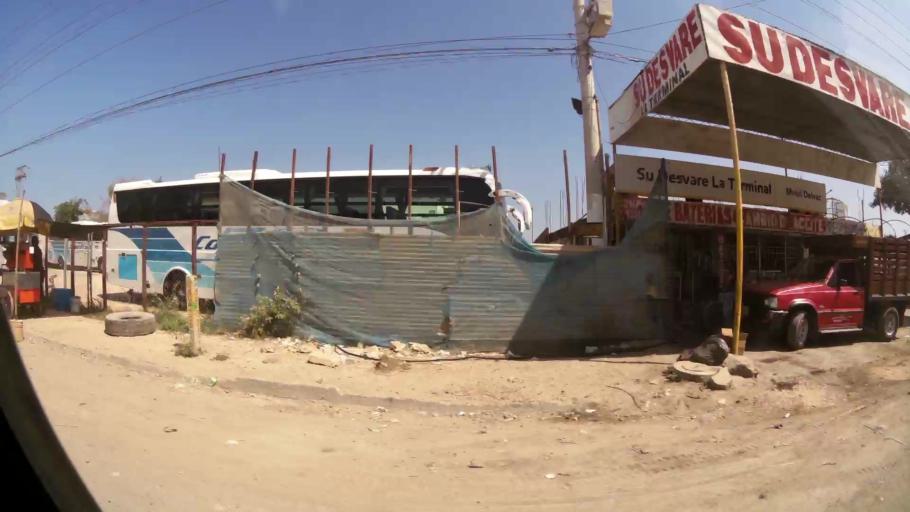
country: CO
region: Bolivar
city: Cartagena
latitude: 10.4015
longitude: -75.4588
